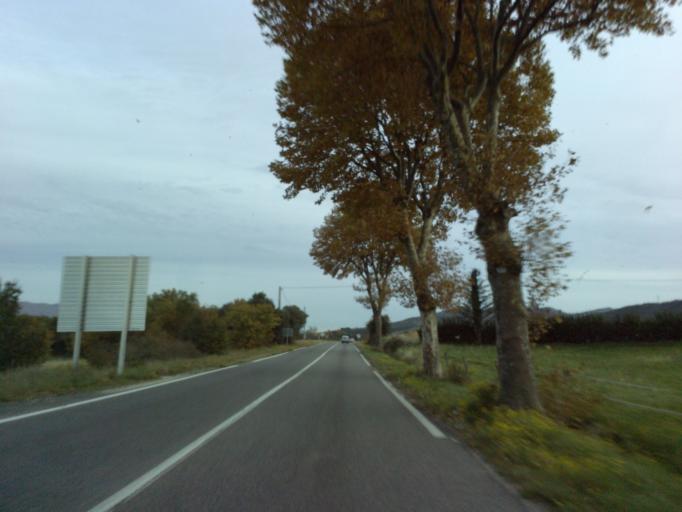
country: FR
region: Provence-Alpes-Cote d'Azur
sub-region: Departement des Alpes-de-Haute-Provence
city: Peipin
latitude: 44.1384
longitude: 5.9686
